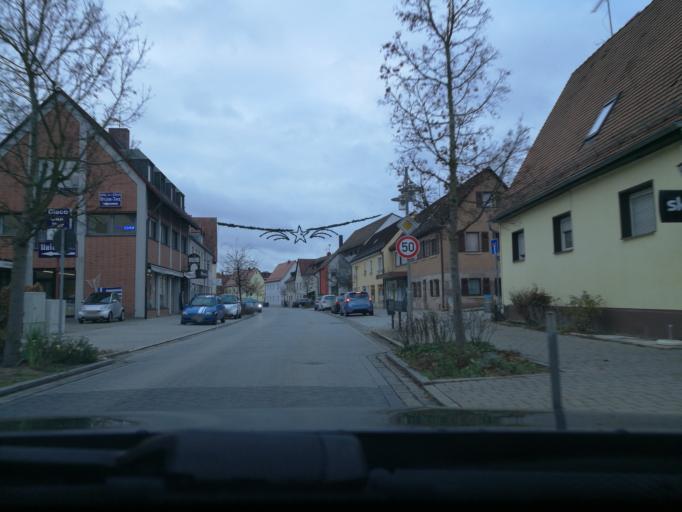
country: DE
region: Bavaria
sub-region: Regierungsbezirk Mittelfranken
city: Heroldsberg
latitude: 49.5314
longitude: 11.1514
